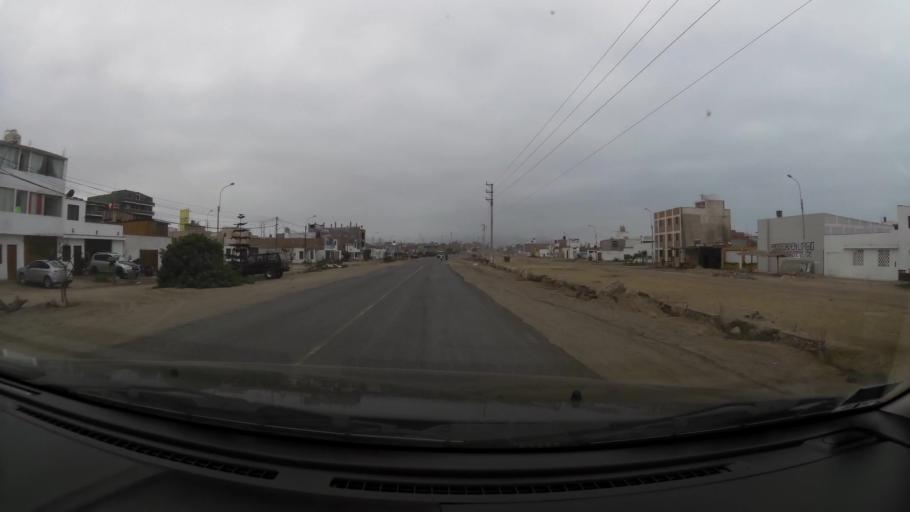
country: PE
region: Lima
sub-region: Lima
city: San Bartolo
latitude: -12.3593
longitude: -76.7993
